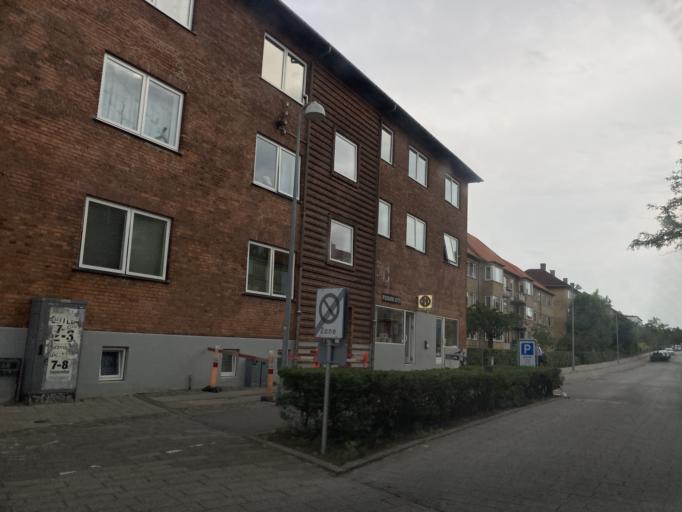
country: DK
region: Capital Region
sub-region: Lyngby-Tarbaek Kommune
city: Kongens Lyngby
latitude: 55.7672
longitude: 12.5021
